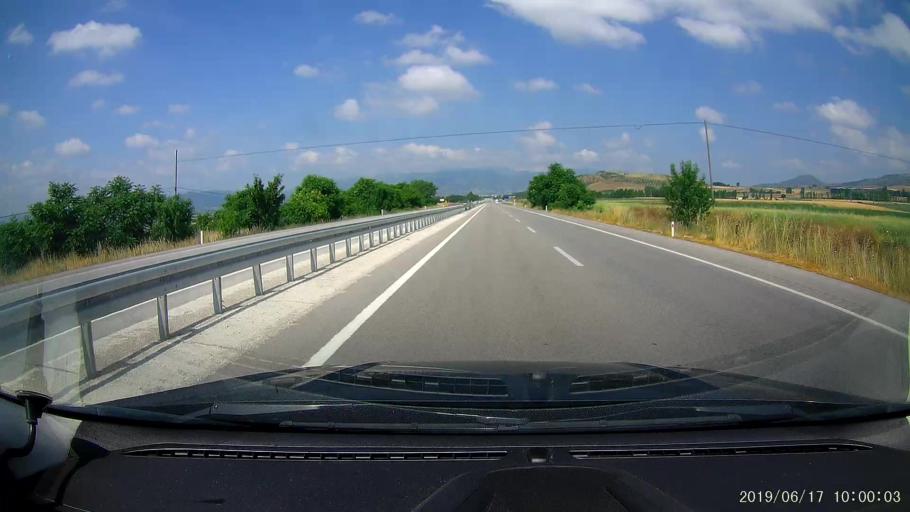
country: TR
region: Amasya
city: Alicik
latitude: 40.8664
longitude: 35.2981
